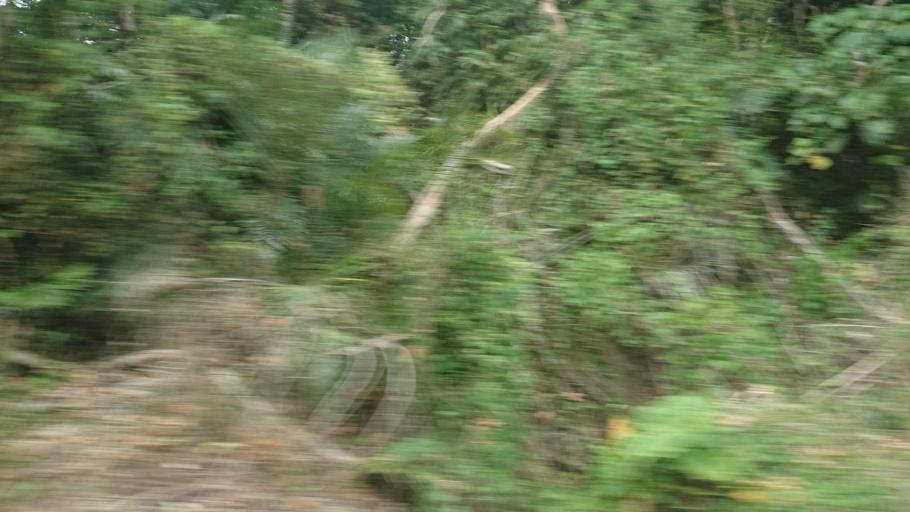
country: TW
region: Taiwan
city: Lugu
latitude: 23.5984
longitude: 120.7005
